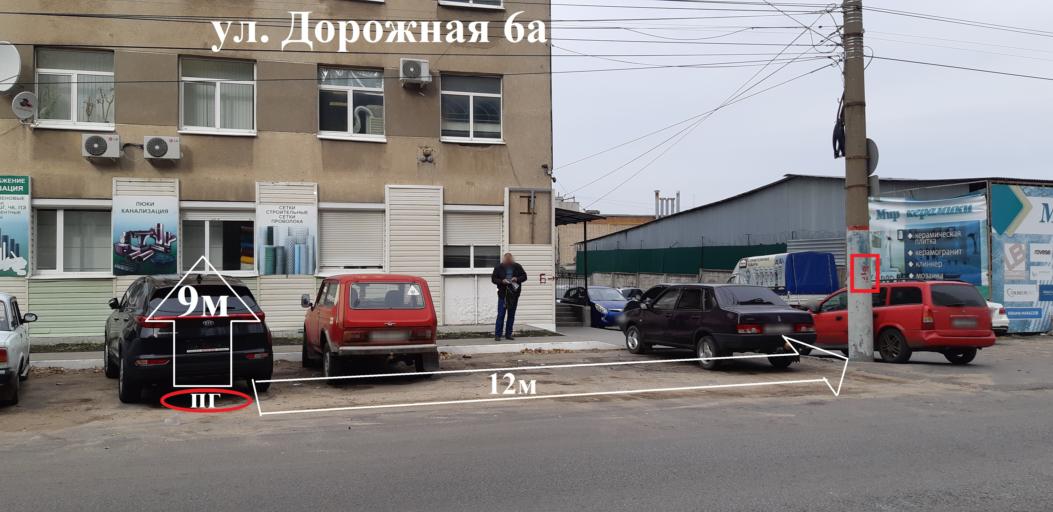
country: RU
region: Voronezj
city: Voronezh
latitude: 51.6638
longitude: 39.1539
